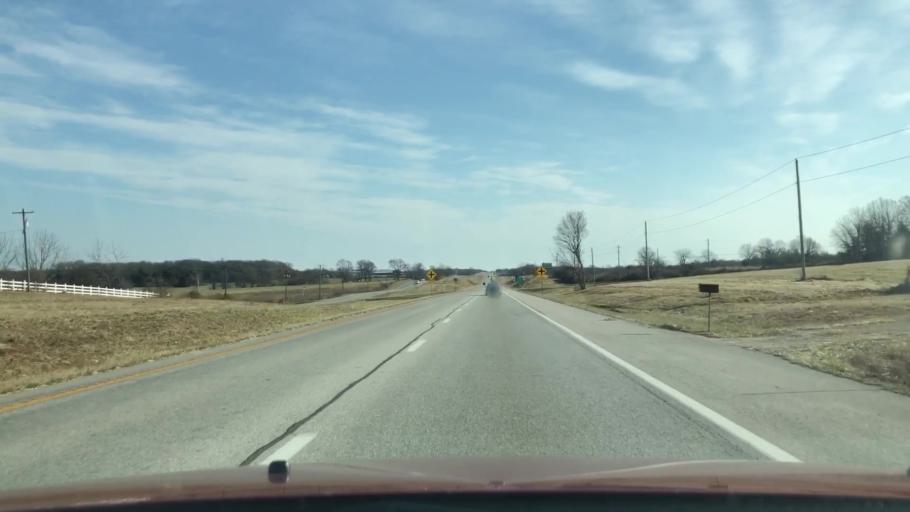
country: US
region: Missouri
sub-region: Webster County
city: Rogersville
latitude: 37.1194
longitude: -93.1585
